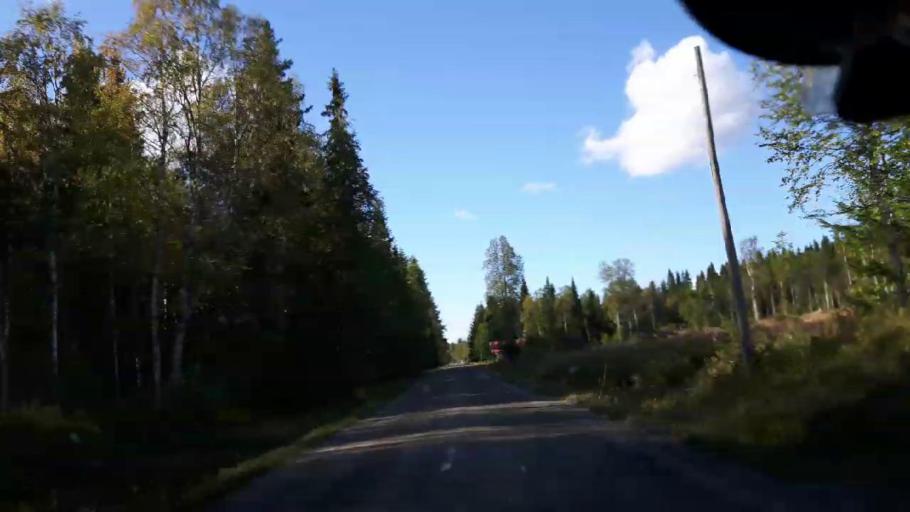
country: SE
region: Jaemtland
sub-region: Ragunda Kommun
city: Hammarstrand
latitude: 63.4694
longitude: 16.1805
